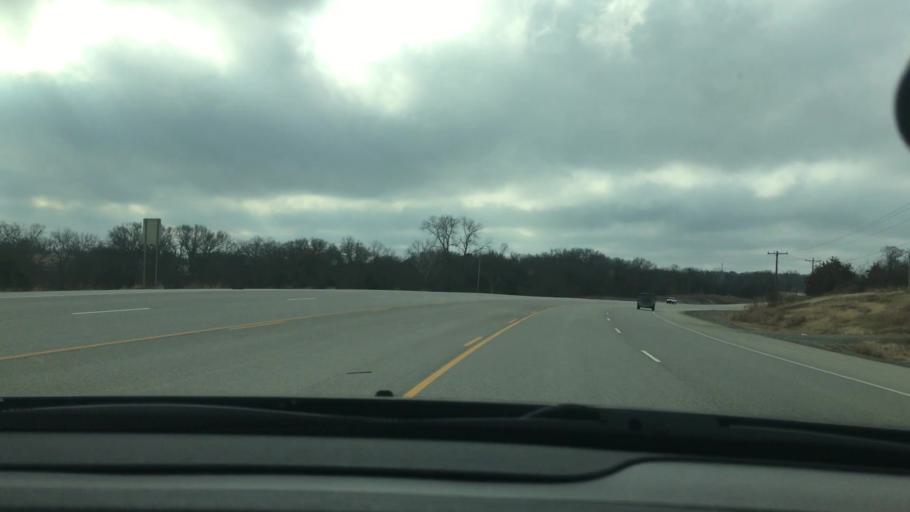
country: US
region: Oklahoma
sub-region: Bryan County
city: Durant
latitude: 34.0508
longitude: -96.3729
